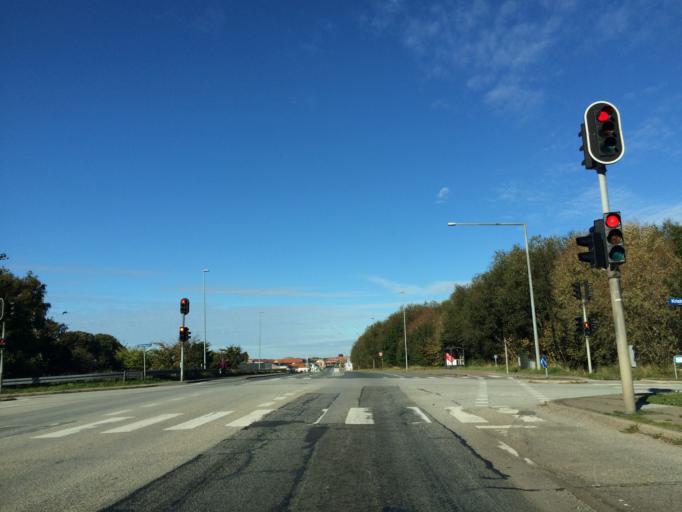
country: DK
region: Central Jutland
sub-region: Randers Kommune
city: Randers
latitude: 56.4505
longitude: 10.0563
